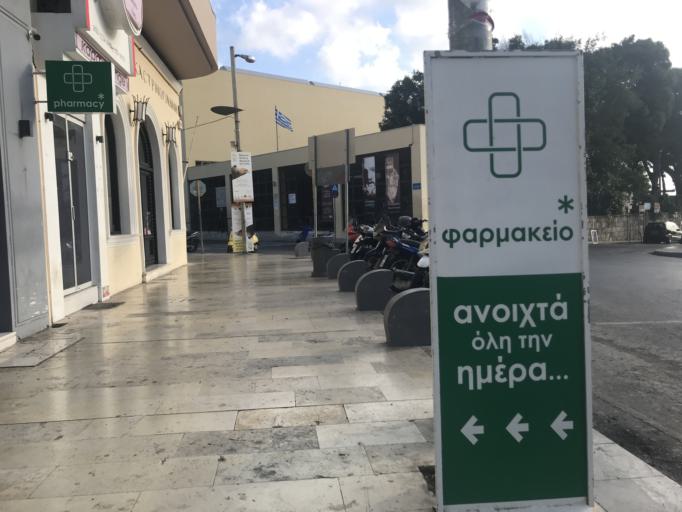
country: GR
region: Crete
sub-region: Nomos Irakleiou
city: Irakleion
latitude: 35.3385
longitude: 25.1366
